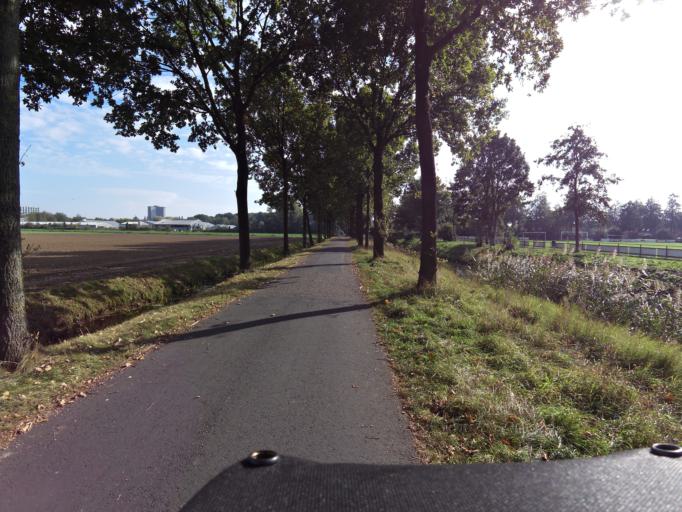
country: NL
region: Gelderland
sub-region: Gemeente Wageningen
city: Wageningen
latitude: 51.9867
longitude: 5.6510
